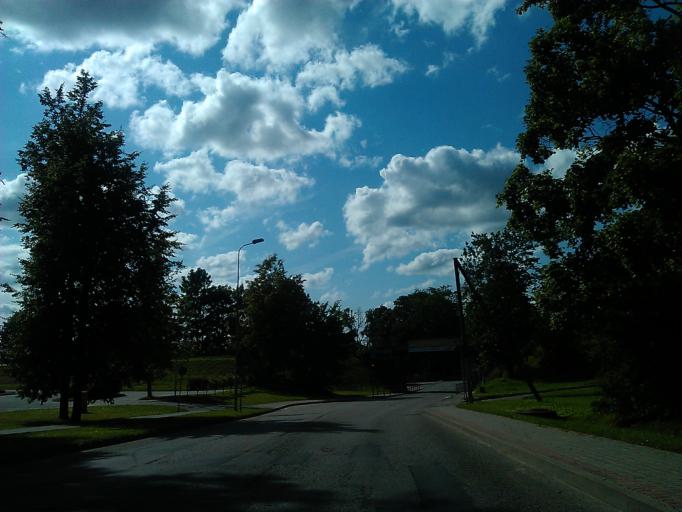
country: LV
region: Cesu Rajons
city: Cesis
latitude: 57.3084
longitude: 25.2790
